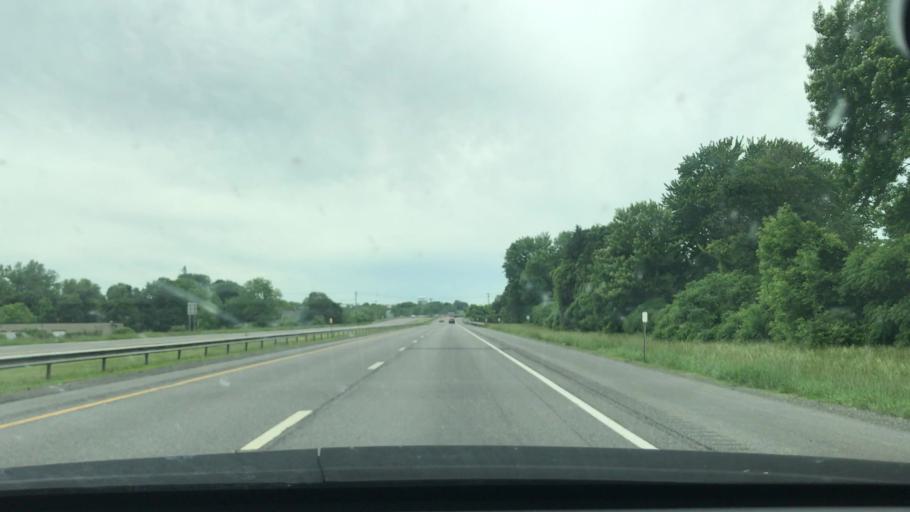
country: US
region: New York
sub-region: Onondaga County
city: Lakeland
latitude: 43.1139
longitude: -76.2531
